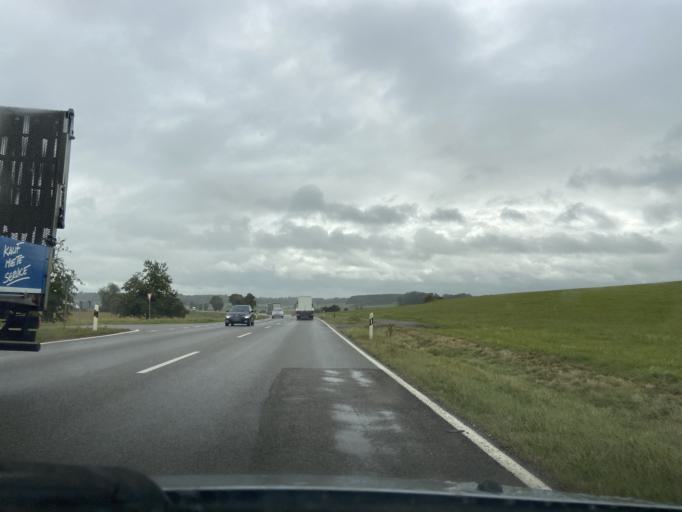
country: DE
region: Baden-Wuerttemberg
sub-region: Tuebingen Region
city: Messkirch
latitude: 48.0039
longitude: 9.1615
